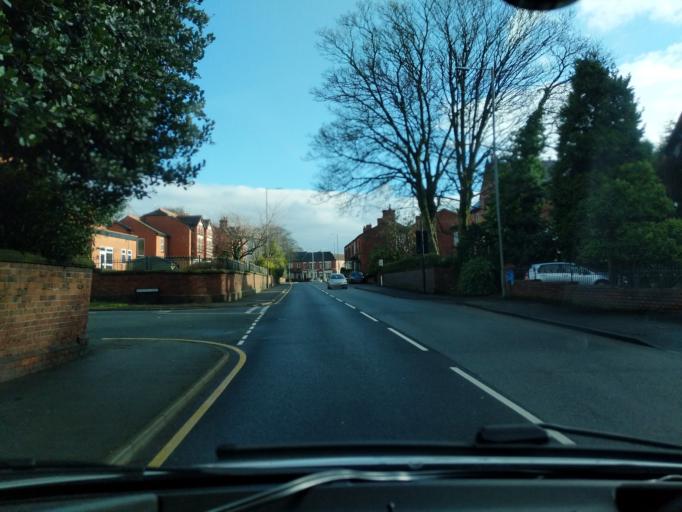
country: GB
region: England
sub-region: St. Helens
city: Eccleston
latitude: 53.4636
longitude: -2.7600
